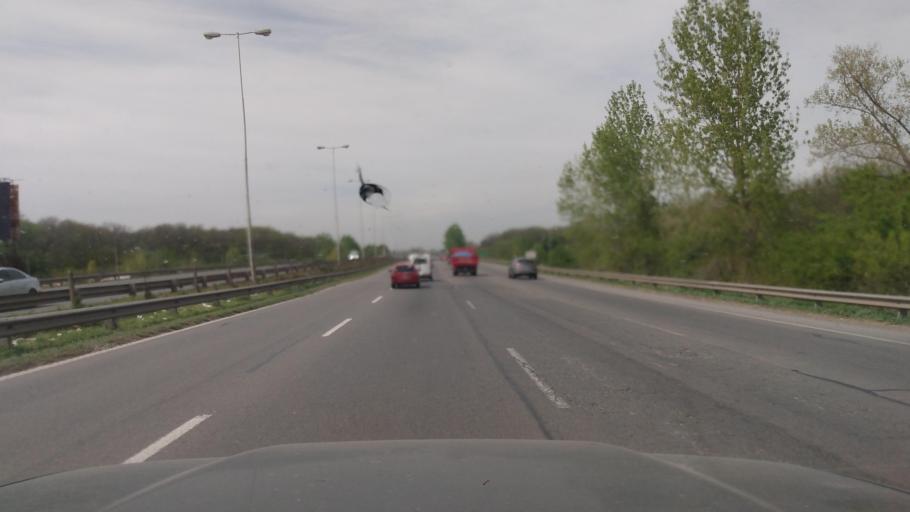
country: AR
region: Buenos Aires
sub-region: Partido de Pilar
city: Pilar
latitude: -34.4453
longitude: -58.9584
